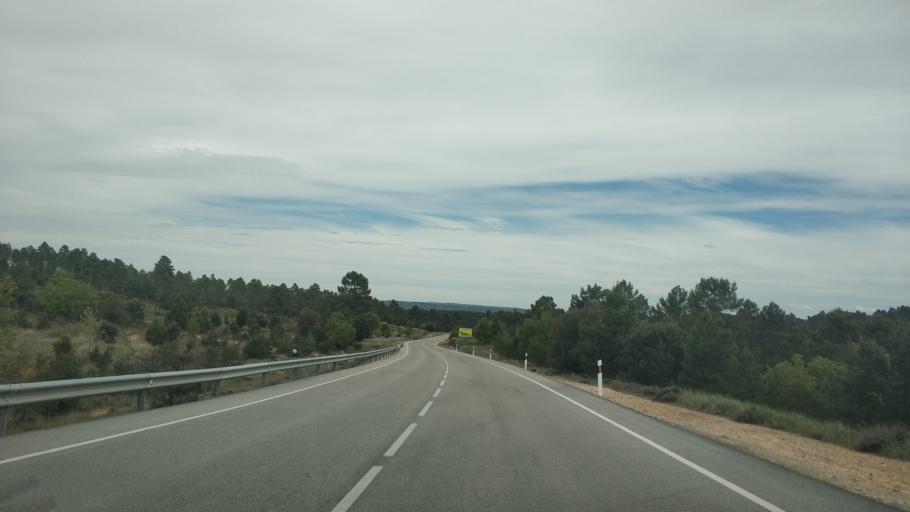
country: ES
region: Castille and Leon
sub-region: Provincia de Soria
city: Quintanas de Gormaz
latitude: 41.5242
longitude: -2.9403
